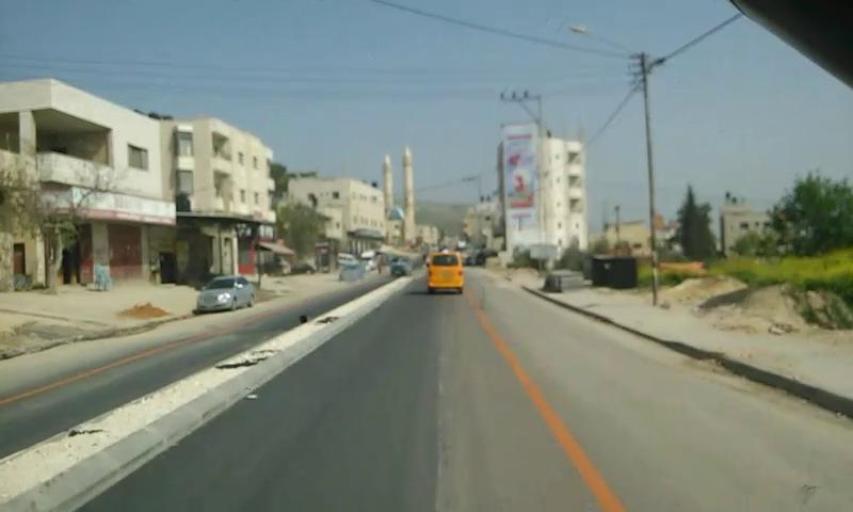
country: PS
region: West Bank
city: Huwwarah
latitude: 32.1552
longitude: 35.2595
